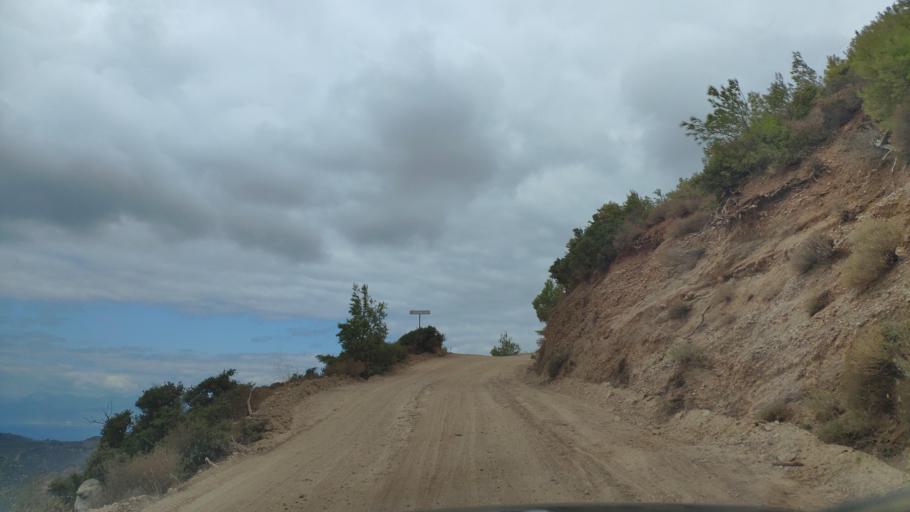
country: GR
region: West Greece
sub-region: Nomos Achaias
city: Temeni
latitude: 38.1658
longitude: 22.1456
